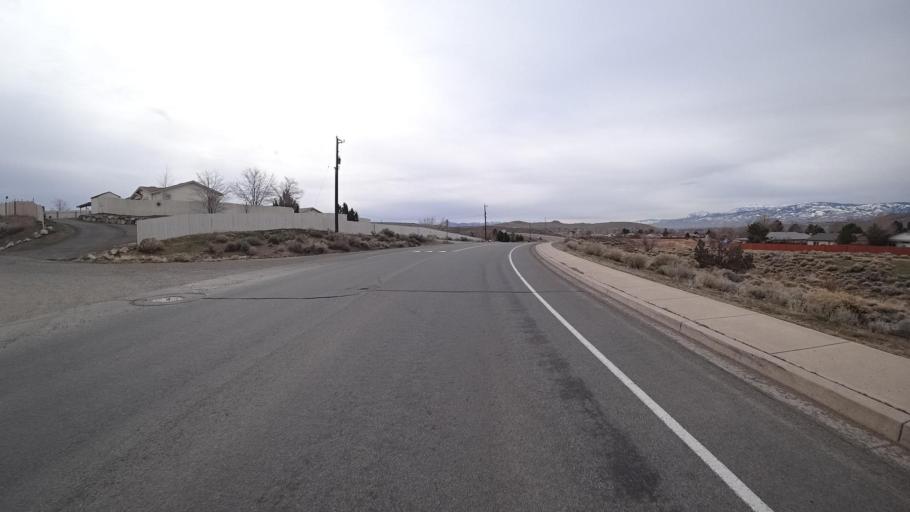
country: US
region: Nevada
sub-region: Washoe County
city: Sun Valley
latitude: 39.6126
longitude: -119.7618
